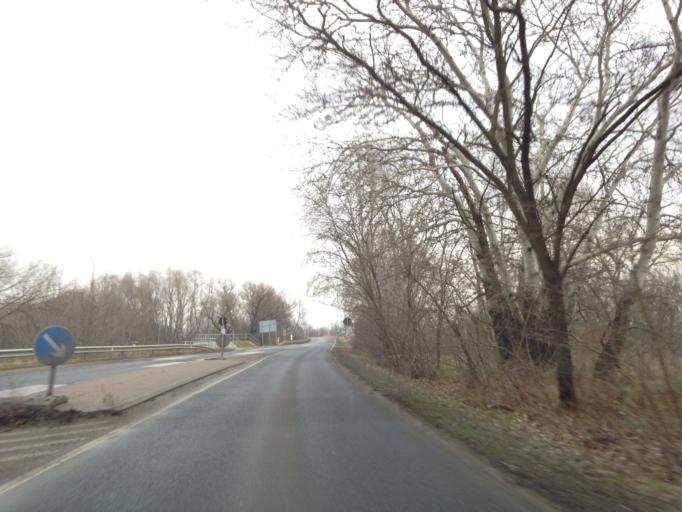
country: HU
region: Komarom-Esztergom
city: Almasfuzito
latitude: 47.7230
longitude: 18.2691
